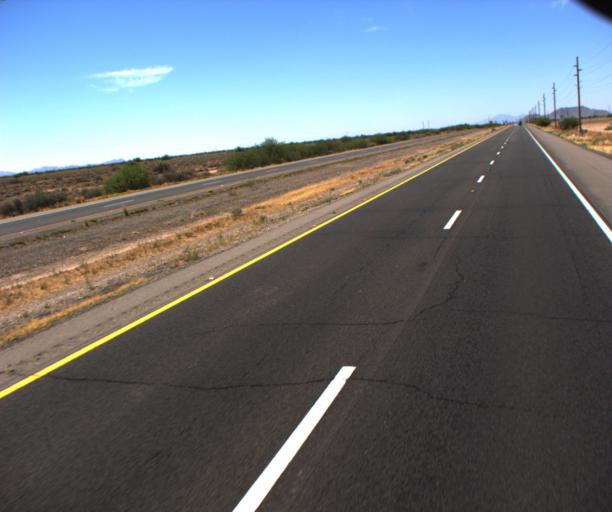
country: US
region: Arizona
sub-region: Maricopa County
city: Sun Lakes
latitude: 33.2276
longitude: -111.9863
